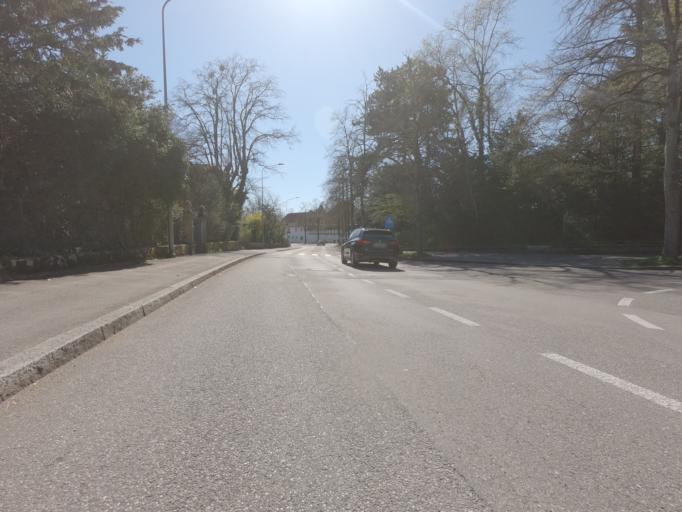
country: CH
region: Solothurn
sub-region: Bezirk Solothurn
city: Solothurn
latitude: 47.2129
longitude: 7.5407
